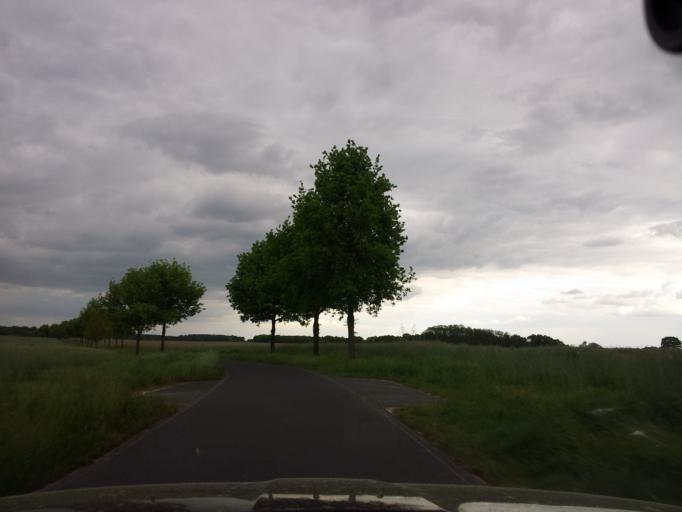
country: DE
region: Brandenburg
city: Niedergorsdorf
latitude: 52.0055
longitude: 12.9427
